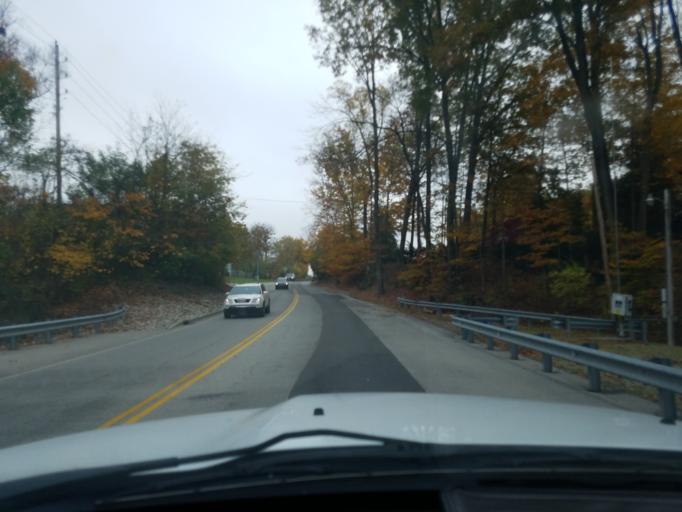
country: US
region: Indiana
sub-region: Clark County
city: Clarksville
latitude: 38.3216
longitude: -85.7806
